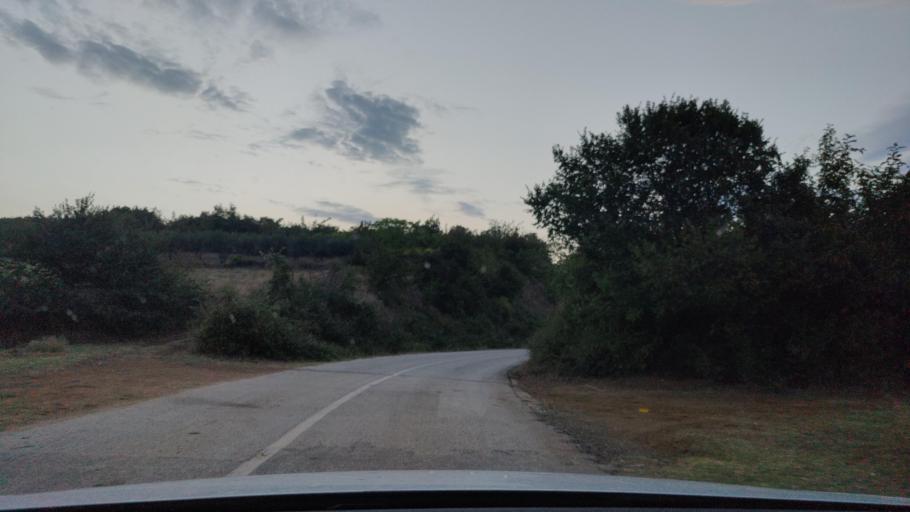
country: GR
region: Central Macedonia
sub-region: Nomos Serron
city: Chrysochorafa
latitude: 41.1424
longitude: 23.2139
